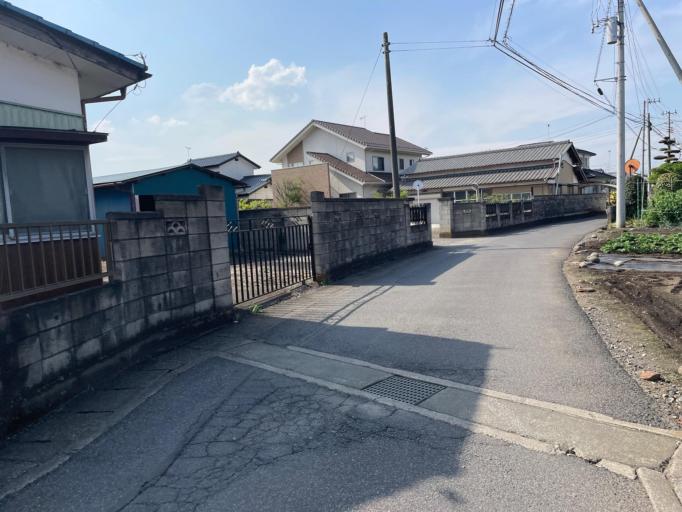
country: JP
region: Gunma
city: Ota
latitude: 36.3058
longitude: 139.4047
